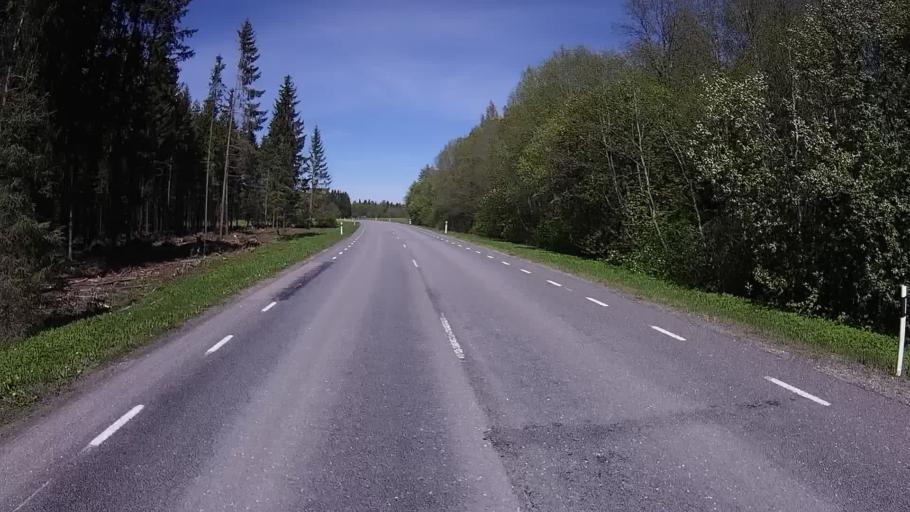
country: EE
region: Raplamaa
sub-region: Kehtna vald
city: Kehtna
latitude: 59.0486
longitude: 25.0236
